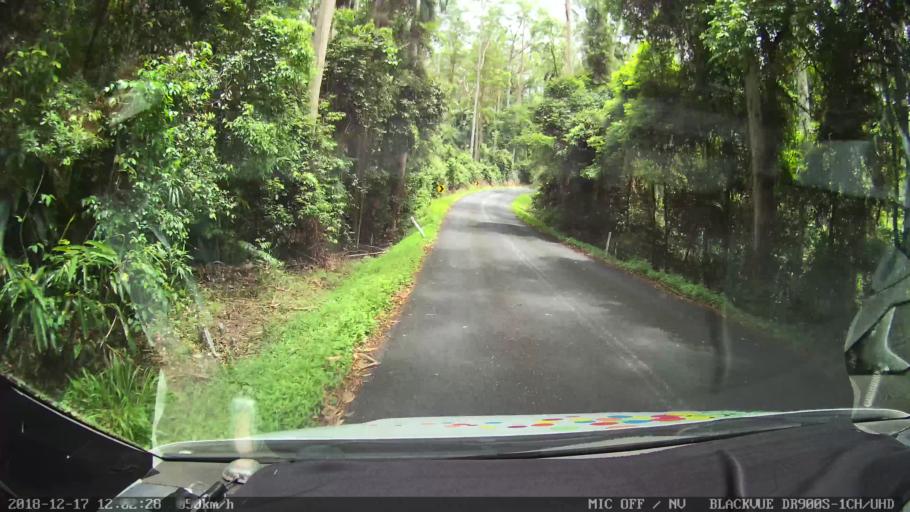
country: AU
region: New South Wales
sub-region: Kyogle
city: Kyogle
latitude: -28.5158
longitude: 152.5684
